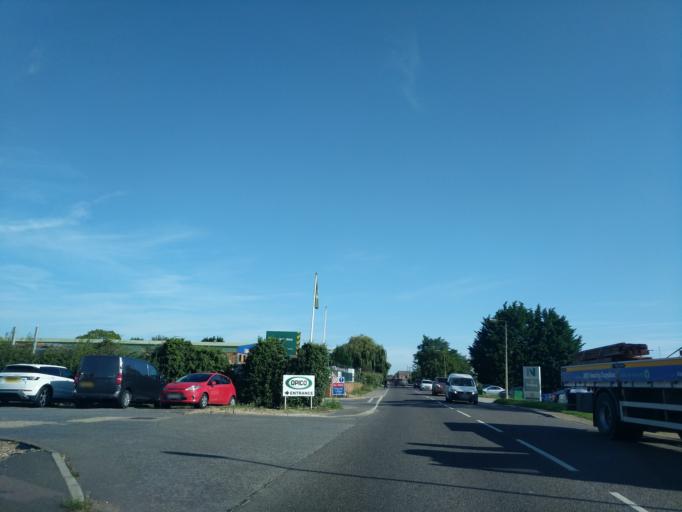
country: GB
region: England
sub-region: Lincolnshire
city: Bourne
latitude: 52.7612
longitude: -0.3624
